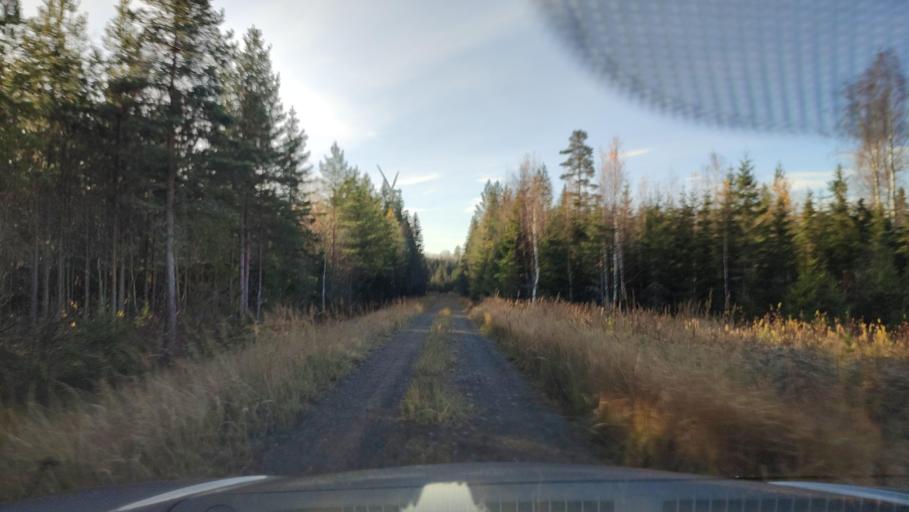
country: FI
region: Southern Ostrobothnia
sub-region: Suupohja
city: Karijoki
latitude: 62.1773
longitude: 21.6076
